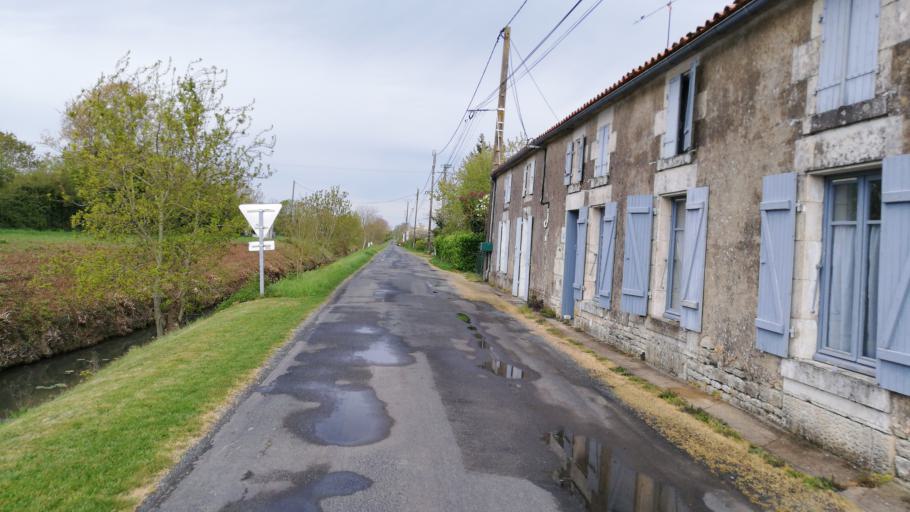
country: FR
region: Pays de la Loire
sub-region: Departement de la Vendee
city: Maillezais
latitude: 46.3273
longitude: -0.7138
